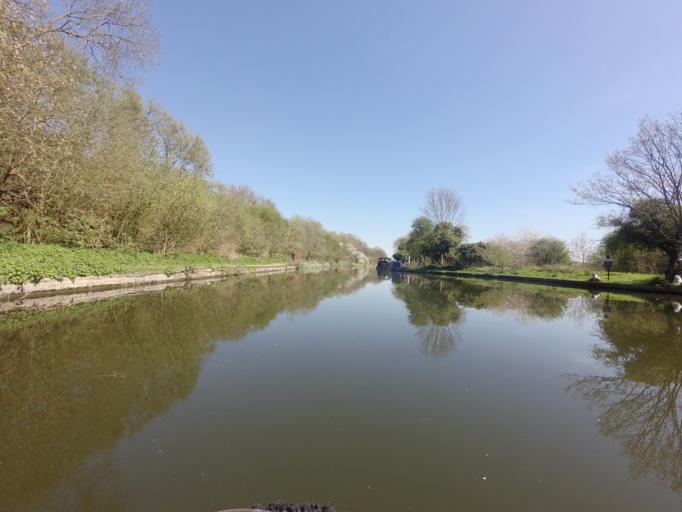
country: GB
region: England
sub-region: Hertfordshire
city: Rickmansworth
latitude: 51.6434
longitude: -0.4417
